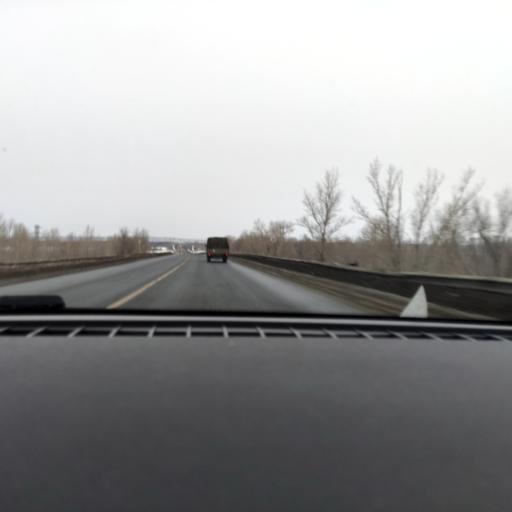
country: RU
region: Samara
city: Kinel'
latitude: 53.1875
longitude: 50.5159
